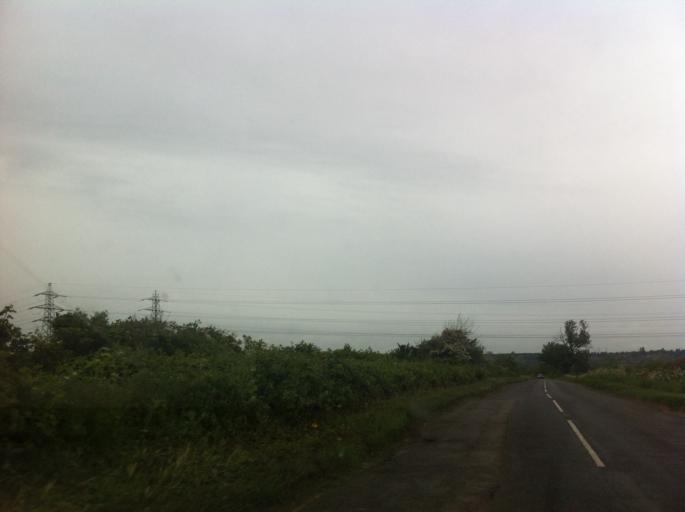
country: GB
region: England
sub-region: Northamptonshire
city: Bozeat
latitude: 52.2601
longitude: -0.6901
